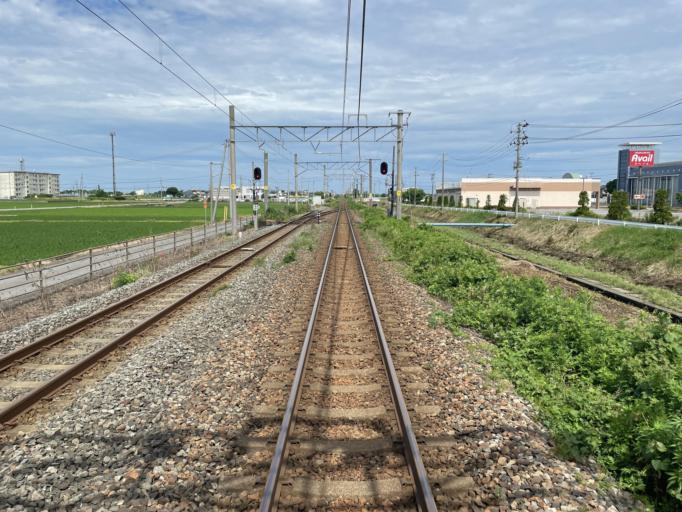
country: JP
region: Niigata
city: Shibata
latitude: 37.9418
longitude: 139.3052
